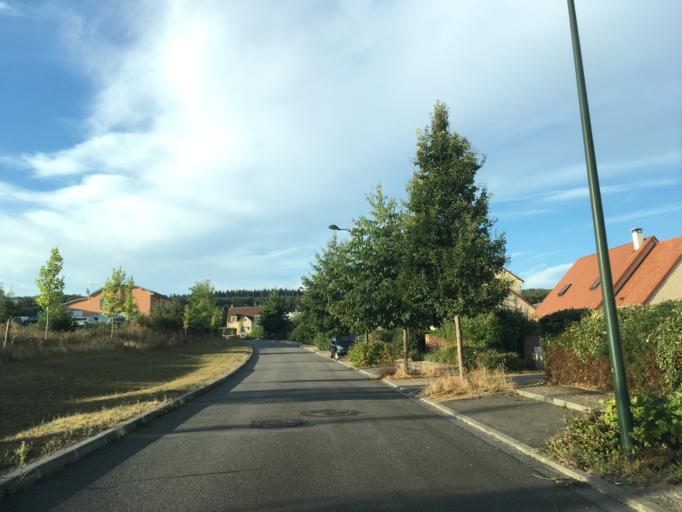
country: FR
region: Haute-Normandie
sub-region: Departement de l'Eure
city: Vernon
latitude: 49.0795
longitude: 1.4981
